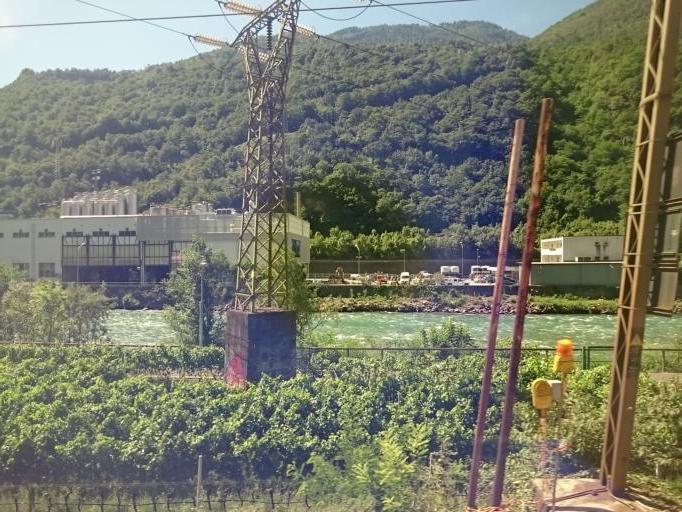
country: IT
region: Trentino-Alto Adige
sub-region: Bolzano
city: Cardano
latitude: 46.4949
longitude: 11.3822
